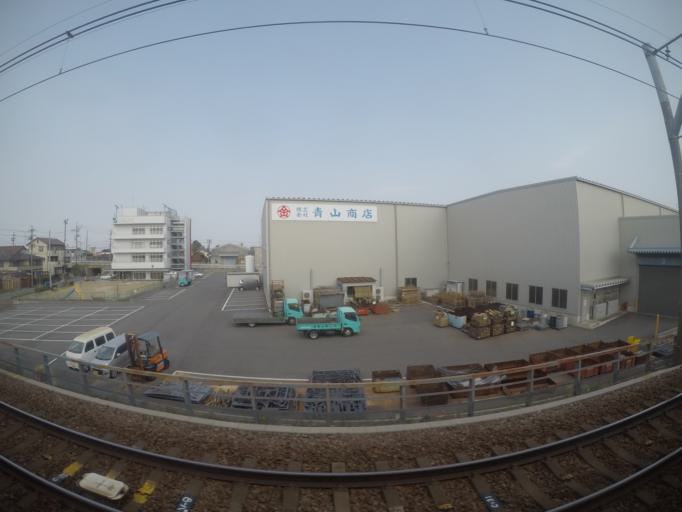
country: JP
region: Aichi
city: Obu
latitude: 35.0664
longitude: 136.9094
